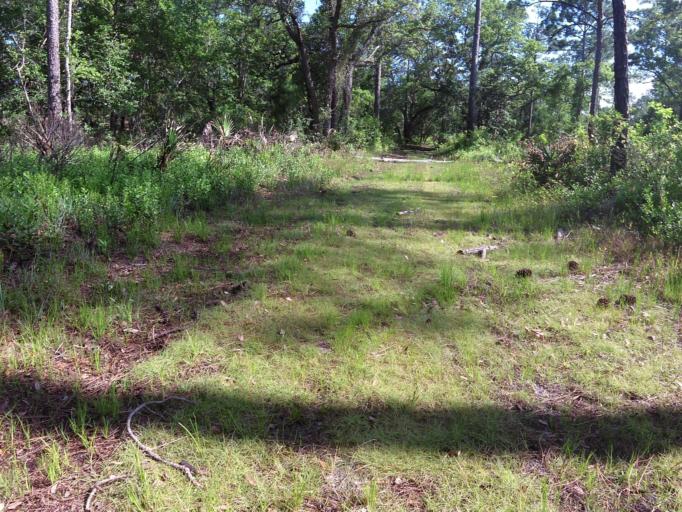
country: US
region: Florida
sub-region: Saint Johns County
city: Palm Valley
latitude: 30.1346
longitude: -81.3716
